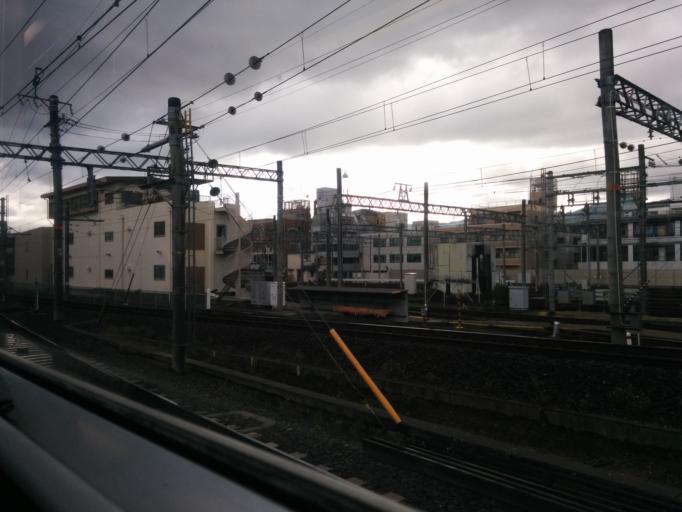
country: JP
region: Kyoto
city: Muko
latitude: 34.9812
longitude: 135.7034
